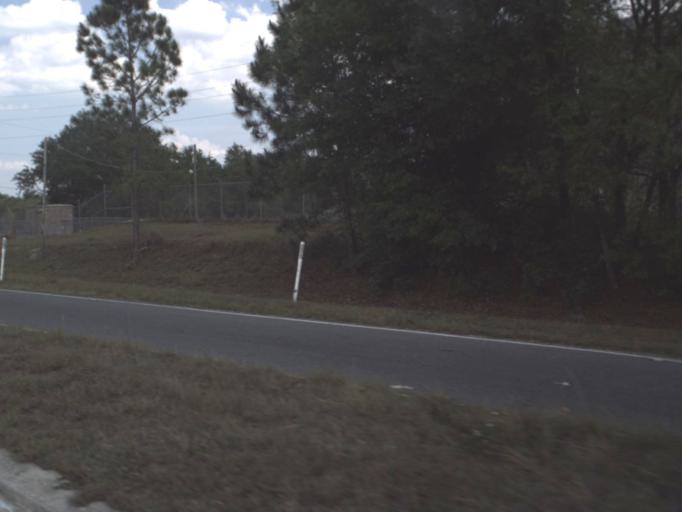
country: US
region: Florida
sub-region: Lake County
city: Howie In The Hills
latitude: 28.6443
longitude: -81.8045
